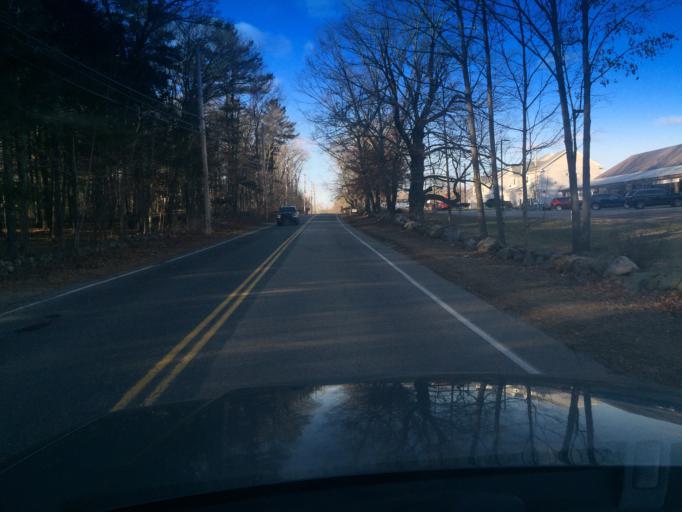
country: US
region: Massachusetts
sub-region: Middlesex County
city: Holliston
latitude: 42.1947
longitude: -71.4179
